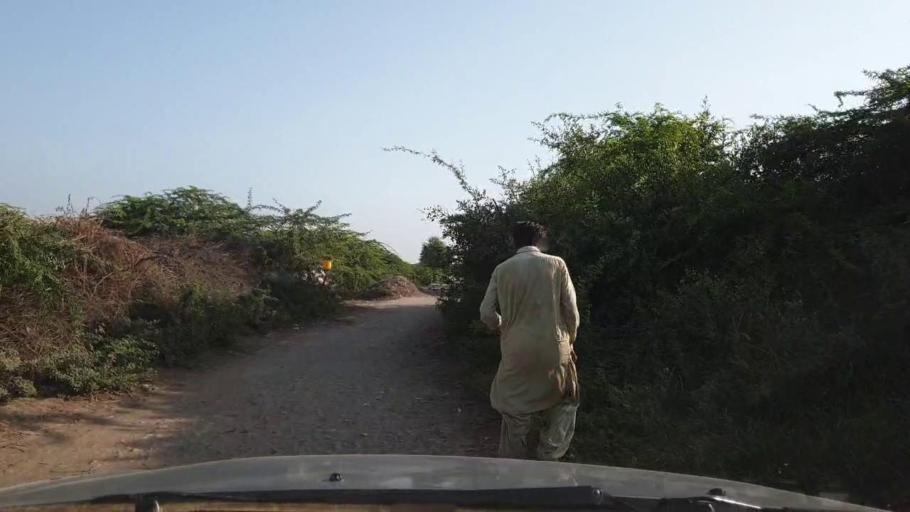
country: PK
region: Sindh
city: Tando Ghulam Ali
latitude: 25.1403
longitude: 68.9428
